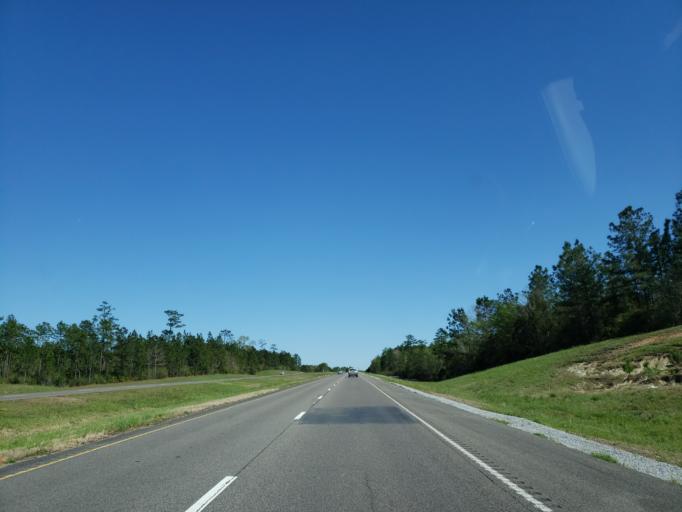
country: US
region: Mississippi
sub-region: Harrison County
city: Saucier
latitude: 30.6061
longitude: -89.0923
